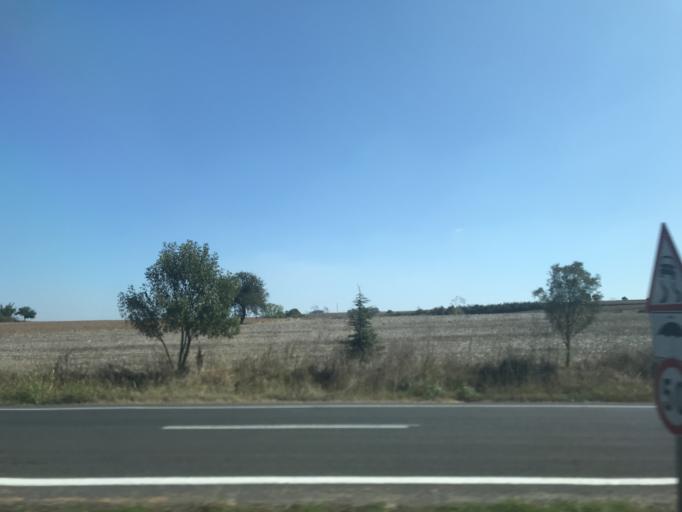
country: TR
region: Tekirdag
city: Muratli
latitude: 41.1382
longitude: 27.4918
